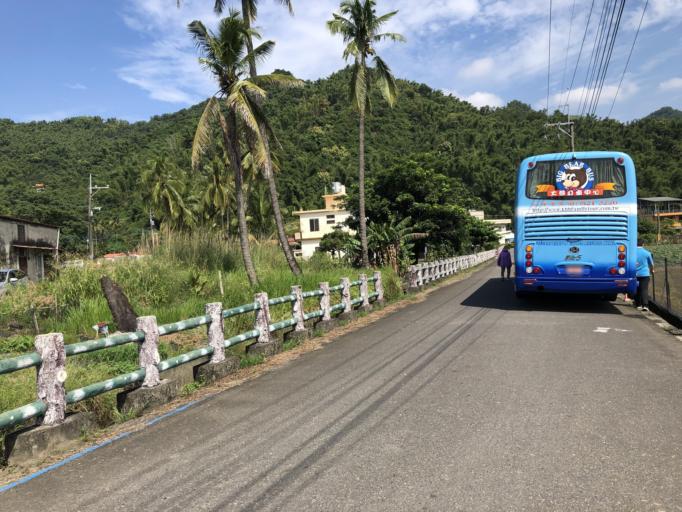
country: TW
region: Taiwan
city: Yujing
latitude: 22.9040
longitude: 120.5239
